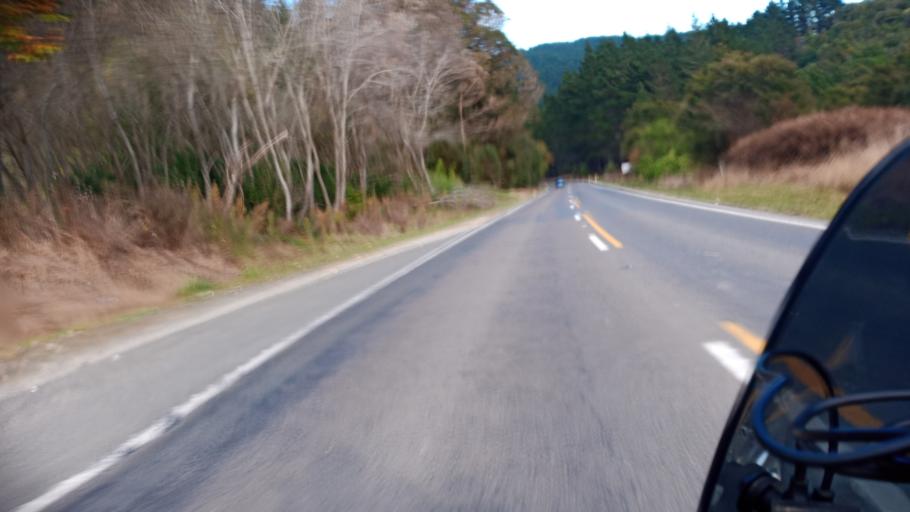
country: NZ
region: Gisborne
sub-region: Gisborne District
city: Gisborne
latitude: -38.8297
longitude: 177.9002
